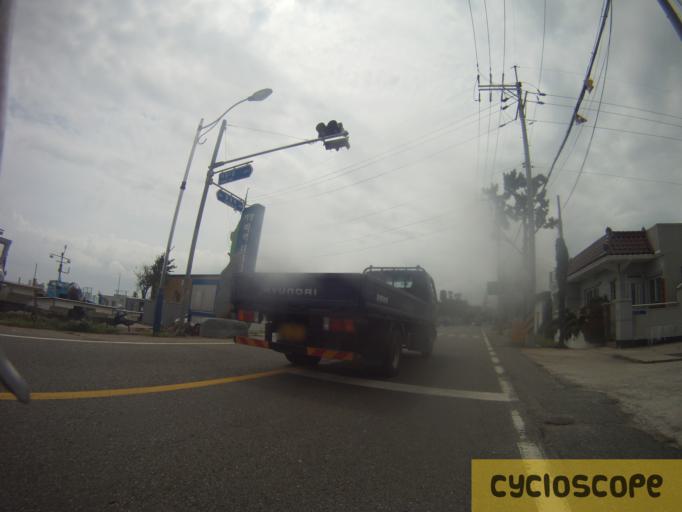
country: KR
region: Busan
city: Kijang
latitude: 35.2687
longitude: 129.2414
